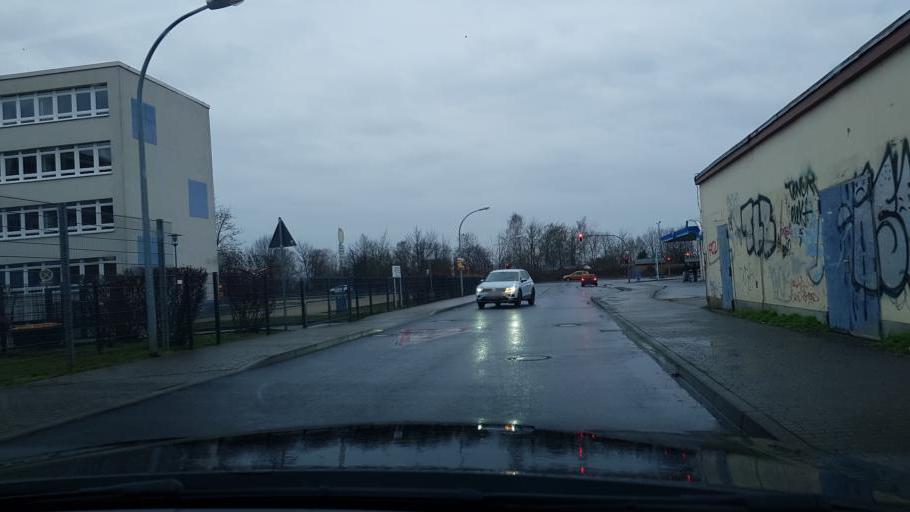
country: DE
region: Berlin
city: Altglienicke
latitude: 52.3958
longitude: 13.5338
